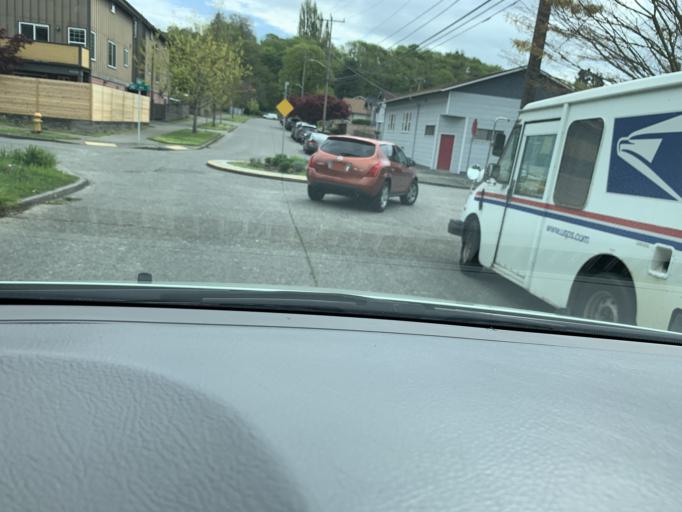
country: US
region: Washington
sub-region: King County
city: White Center
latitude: 47.5534
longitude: -122.3126
